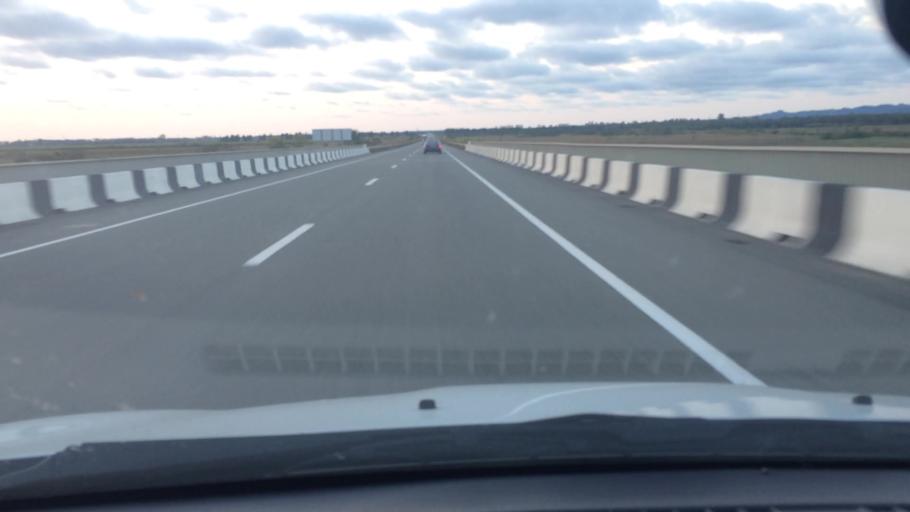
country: GE
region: Ajaria
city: Ochkhamuri
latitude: 41.8712
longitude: 41.8306
